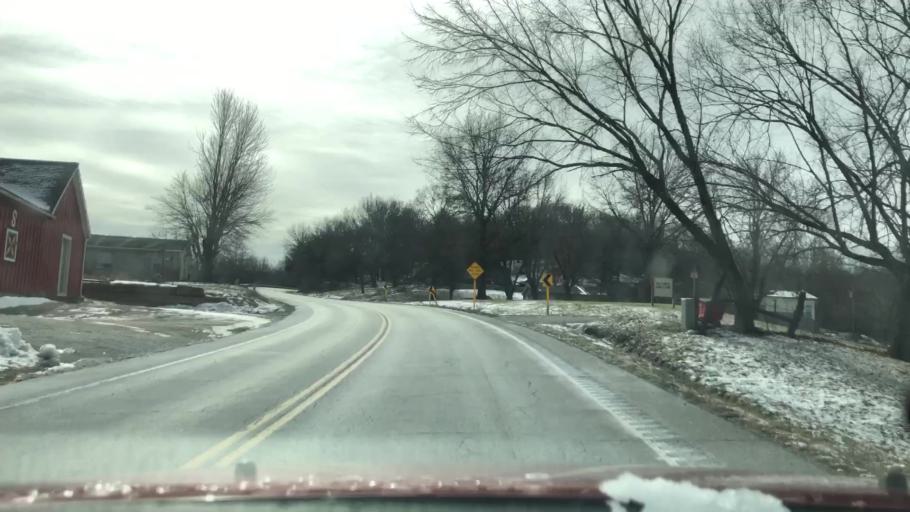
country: US
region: Missouri
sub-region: Jackson County
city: Oak Grove
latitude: 38.9400
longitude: -94.1326
